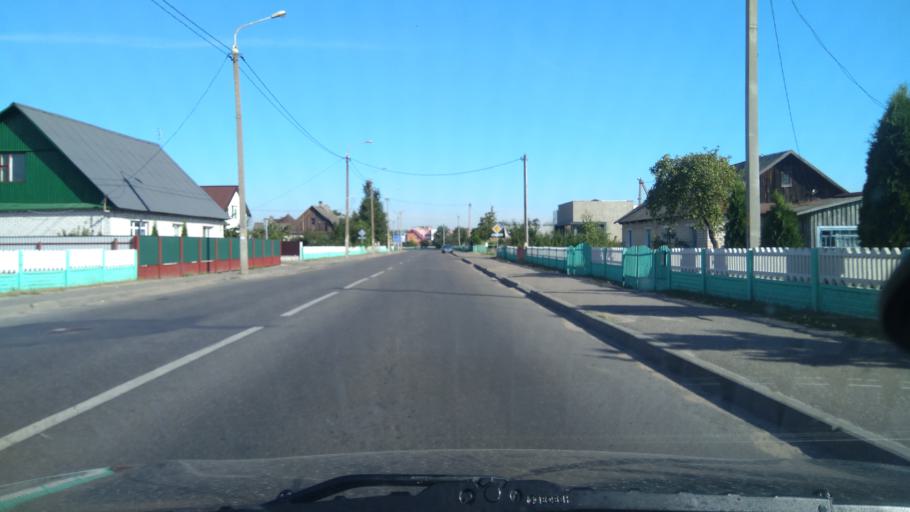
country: BY
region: Brest
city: Ivatsevichy
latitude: 52.7087
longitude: 25.3348
